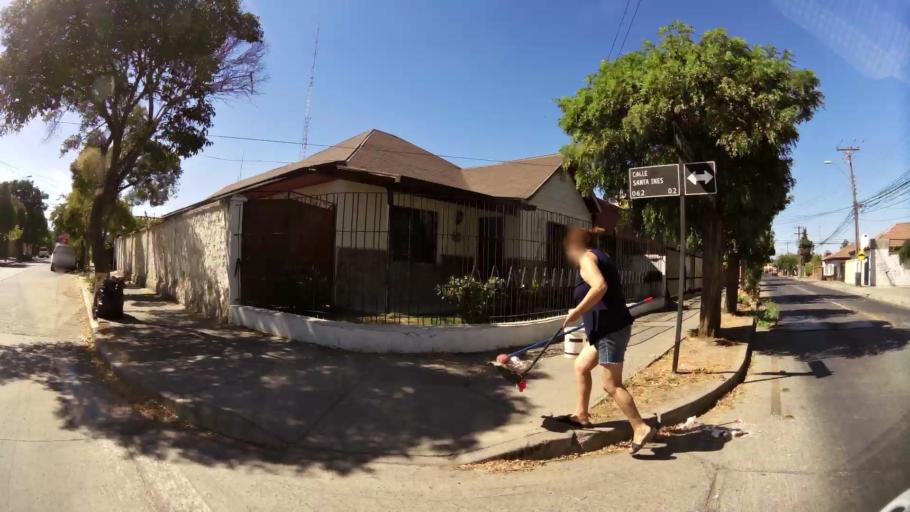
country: CL
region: O'Higgins
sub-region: Provincia de Cachapoal
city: Rancagua
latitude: -34.1785
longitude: -70.7369
